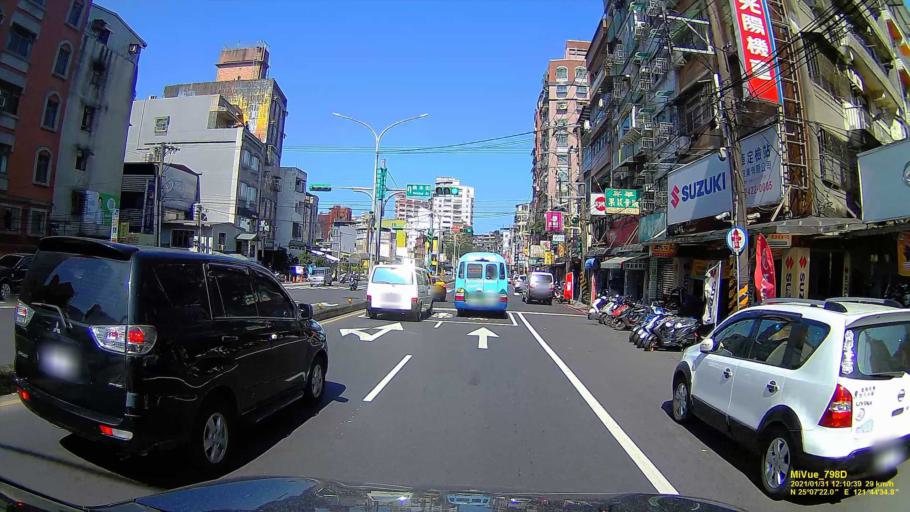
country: TW
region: Taiwan
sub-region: Keelung
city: Keelung
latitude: 25.1229
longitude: 121.7430
